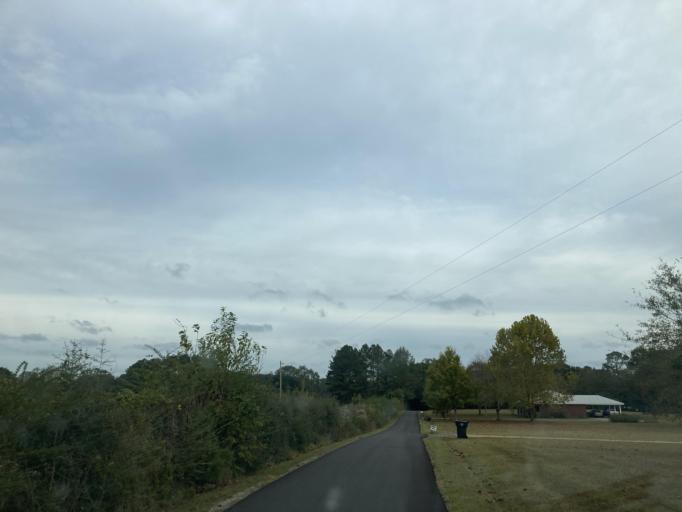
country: US
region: Mississippi
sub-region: Lamar County
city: Purvis
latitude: 31.1235
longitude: -89.4843
